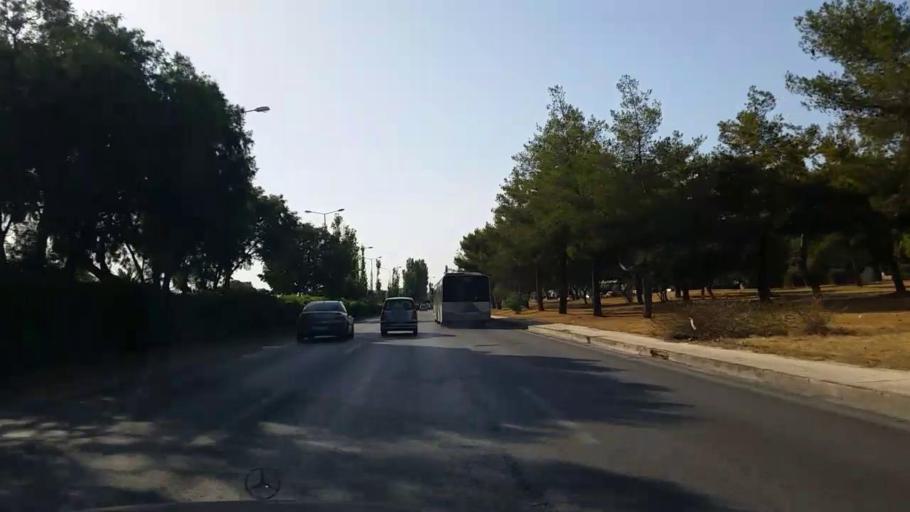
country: GR
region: Attica
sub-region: Nomarchia Athinas
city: Glyfada
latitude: 37.8442
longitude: 23.7564
